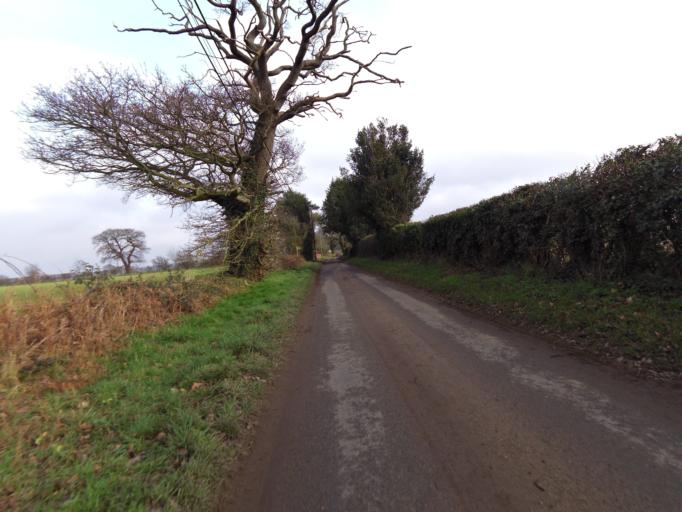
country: GB
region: England
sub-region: Suffolk
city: Woodbridge
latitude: 52.0695
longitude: 1.2971
